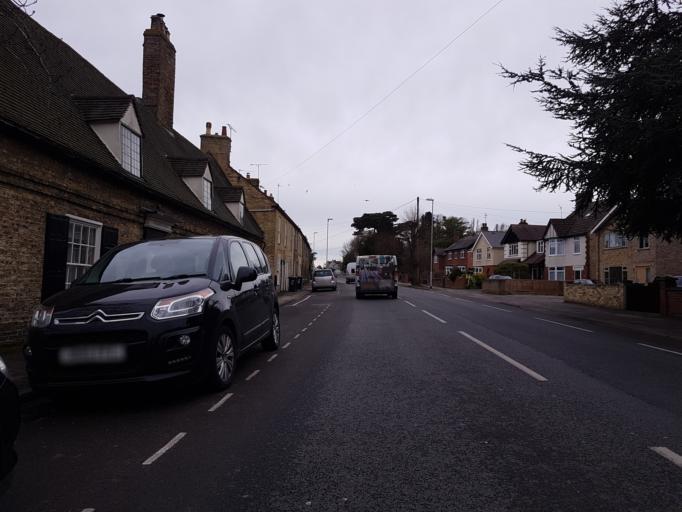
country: GB
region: England
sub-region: Cambridgeshire
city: Ely
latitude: 52.3974
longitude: 0.2558
